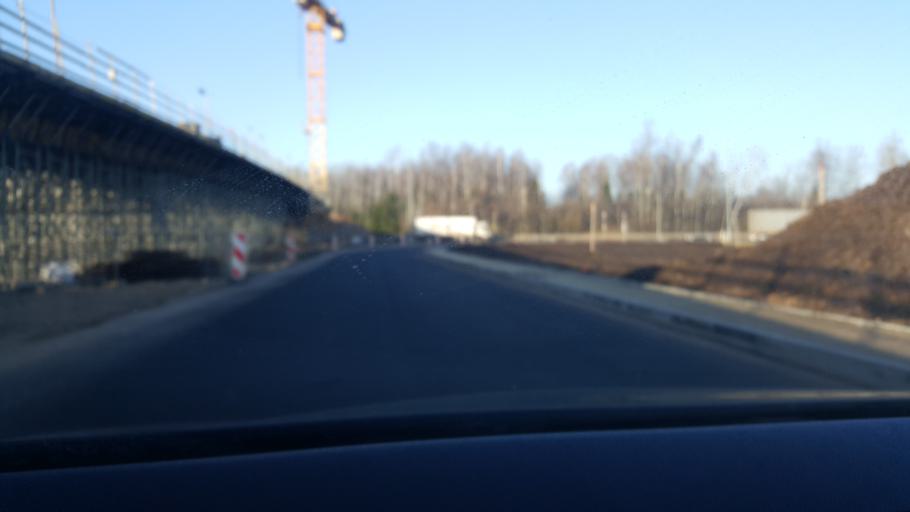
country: LT
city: Ramuciai
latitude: 54.9428
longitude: 24.0073
